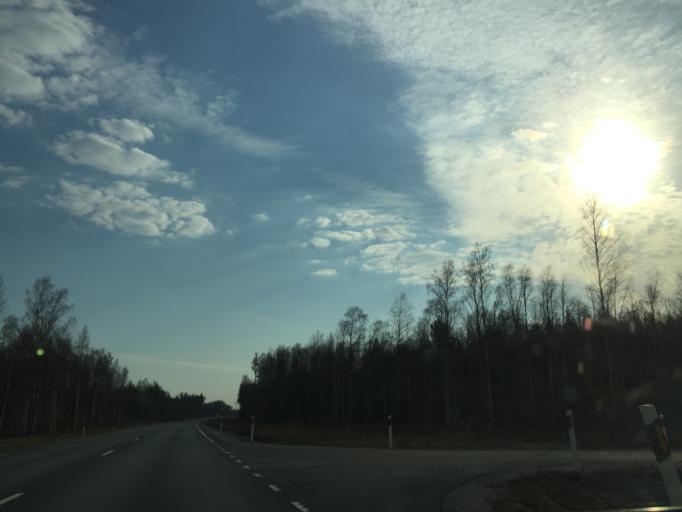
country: EE
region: Jogevamaa
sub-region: Mustvee linn
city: Mustvee
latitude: 58.8659
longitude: 26.9359
